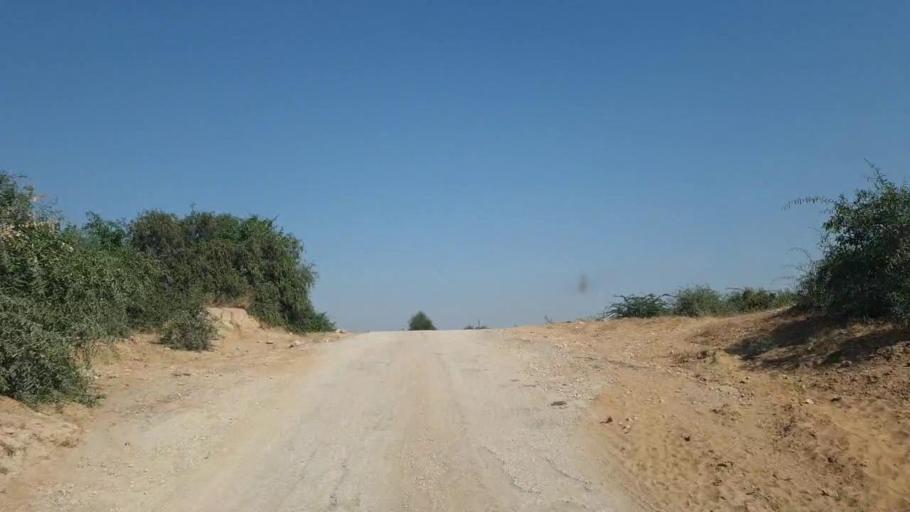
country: PK
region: Sindh
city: Gharo
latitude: 25.1785
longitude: 67.7344
